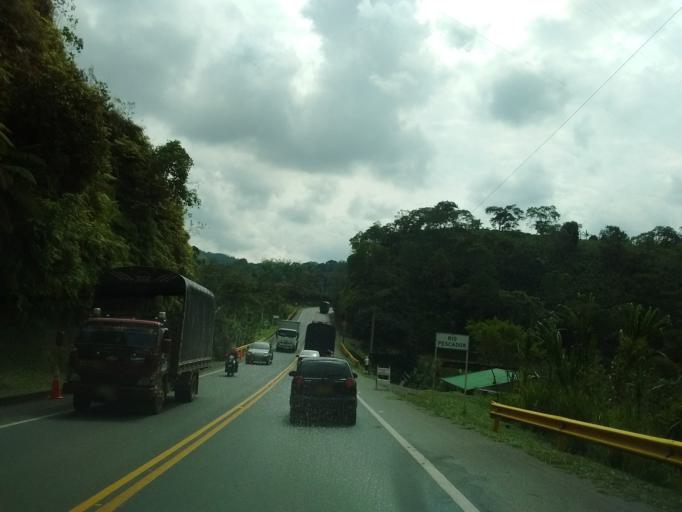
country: CO
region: Cauca
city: Caldono
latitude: 2.7940
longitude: -76.5525
